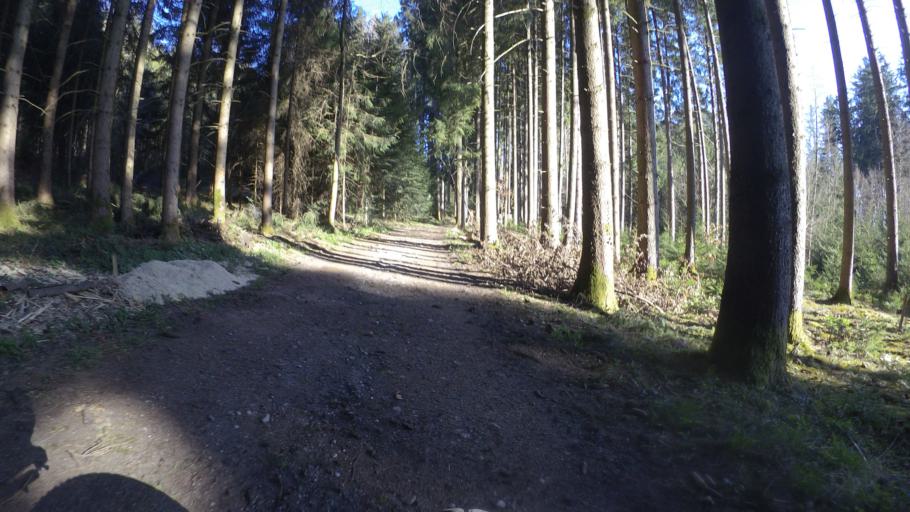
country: DE
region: Bavaria
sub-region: Upper Bavaria
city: Chieming
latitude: 47.9336
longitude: 12.5450
